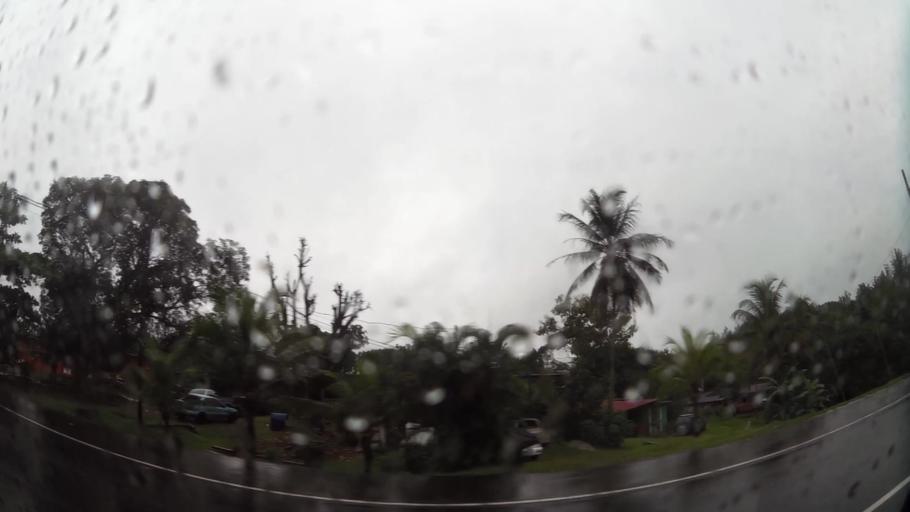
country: PA
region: Colon
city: Santa Rita Arriba
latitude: 9.3184
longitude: -79.7959
